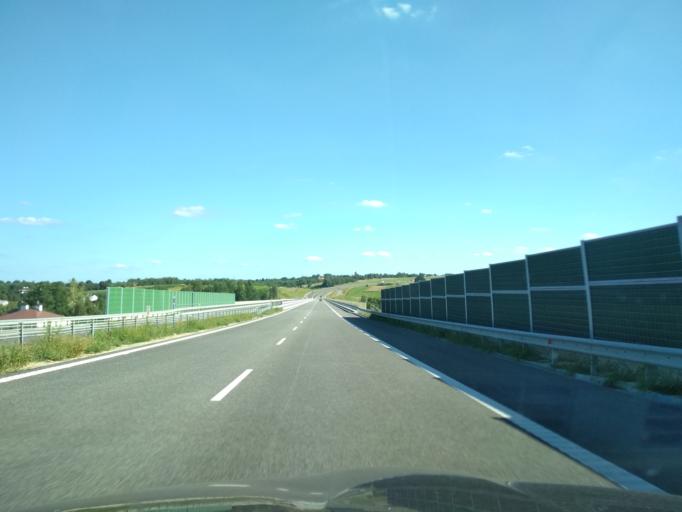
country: PL
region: Subcarpathian Voivodeship
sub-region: Rzeszow
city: Przybyszowka
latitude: 50.0506
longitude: 21.9273
